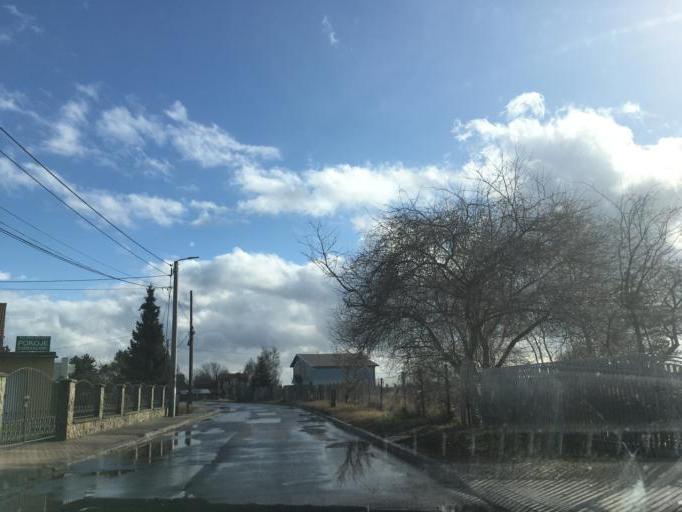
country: PL
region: Pomeranian Voivodeship
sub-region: Powiat gdanski
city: Cedry Wielkie
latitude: 54.3477
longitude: 18.8116
